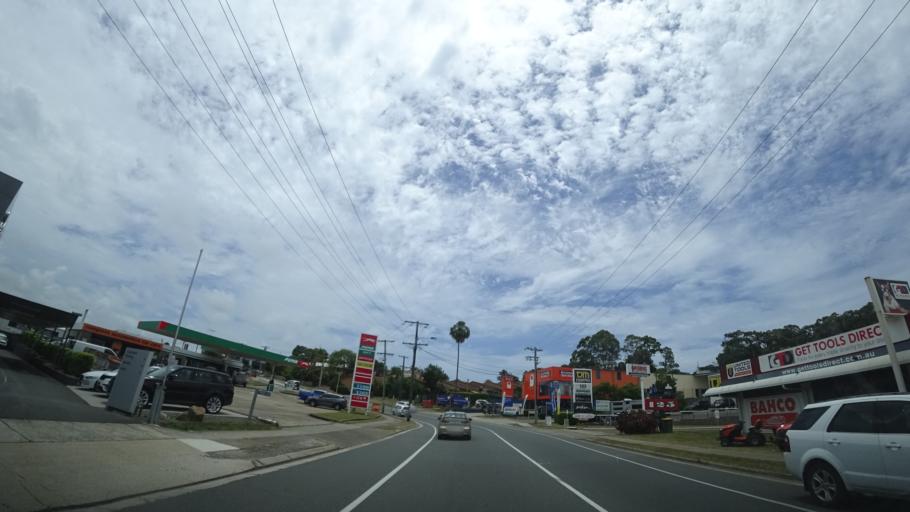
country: AU
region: Queensland
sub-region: Sunshine Coast
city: Mooloolaba
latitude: -26.6714
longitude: 153.0956
